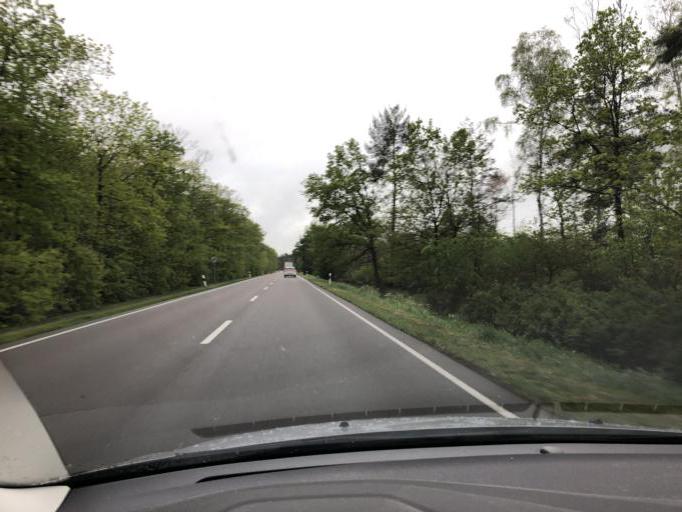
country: DE
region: Saxony-Anhalt
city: Dessau
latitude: 51.7702
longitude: 12.2306
